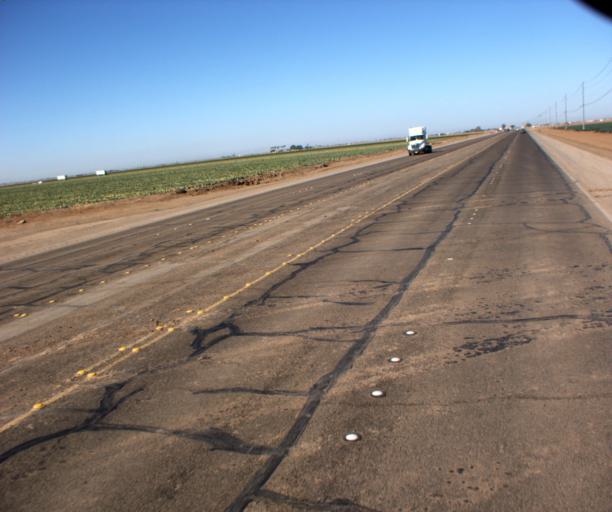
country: US
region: Arizona
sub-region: Yuma County
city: Somerton
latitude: 32.5967
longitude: -114.7482
